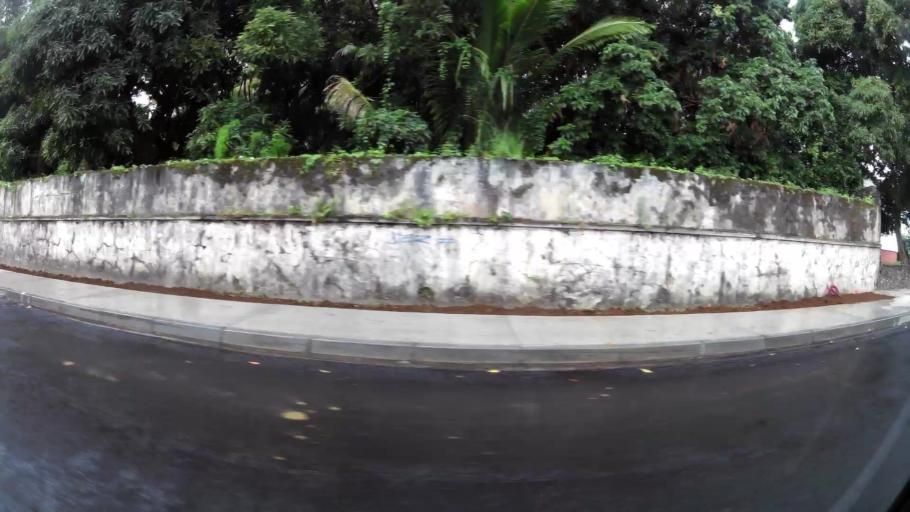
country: RE
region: Reunion
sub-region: Reunion
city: Saint-Andre
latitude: -20.9322
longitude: 55.6410
